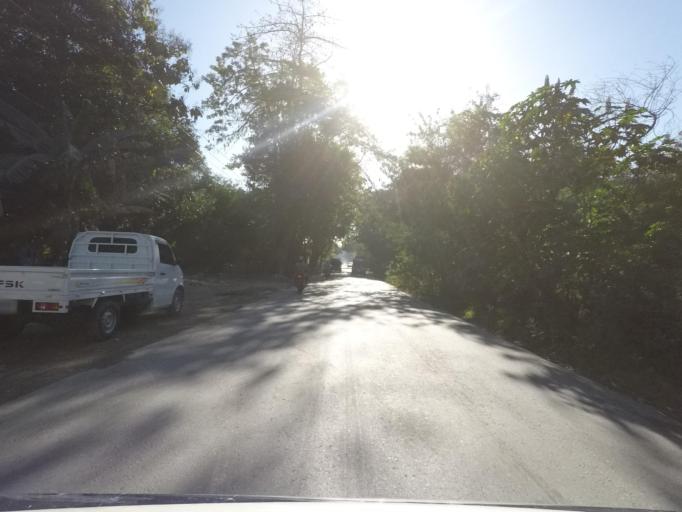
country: ID
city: Metinaro
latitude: -8.5502
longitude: 125.6634
